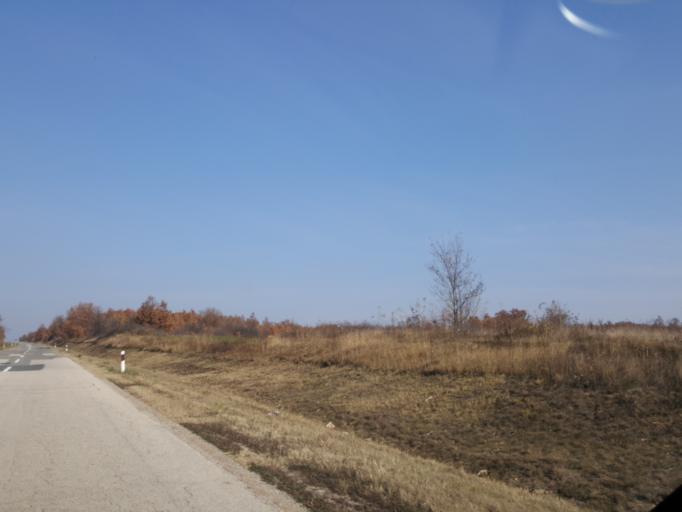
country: RS
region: Central Serbia
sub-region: Borski Okrug
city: Negotin
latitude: 44.1558
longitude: 22.3592
